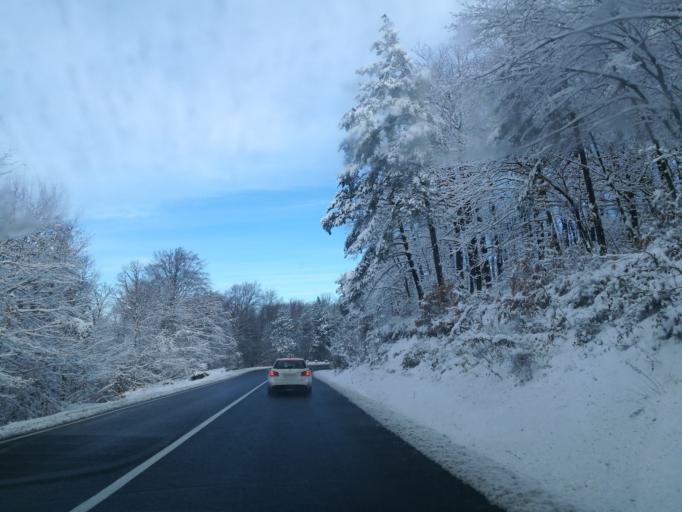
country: RO
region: Brasov
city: Brasov
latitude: 45.6414
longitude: 25.5614
